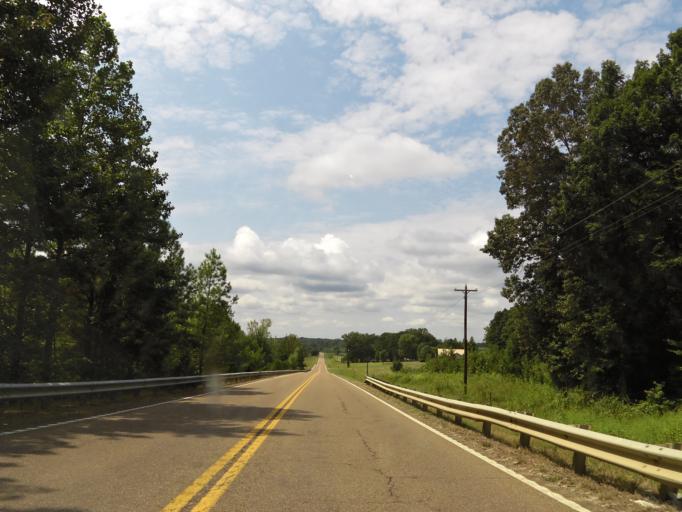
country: US
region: Tennessee
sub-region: Henderson County
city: Lexington
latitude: 35.5017
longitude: -88.3582
